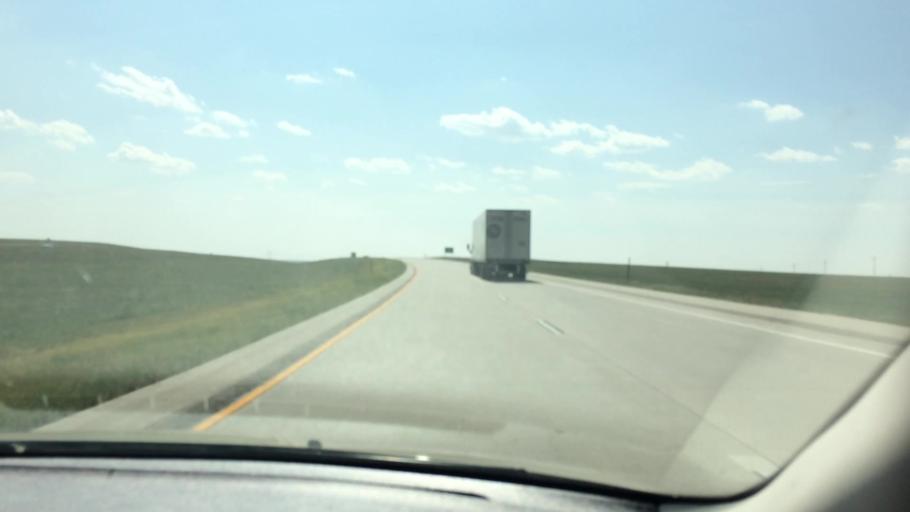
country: US
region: Colorado
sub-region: Lincoln County
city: Limon
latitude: 39.2674
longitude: -103.6298
